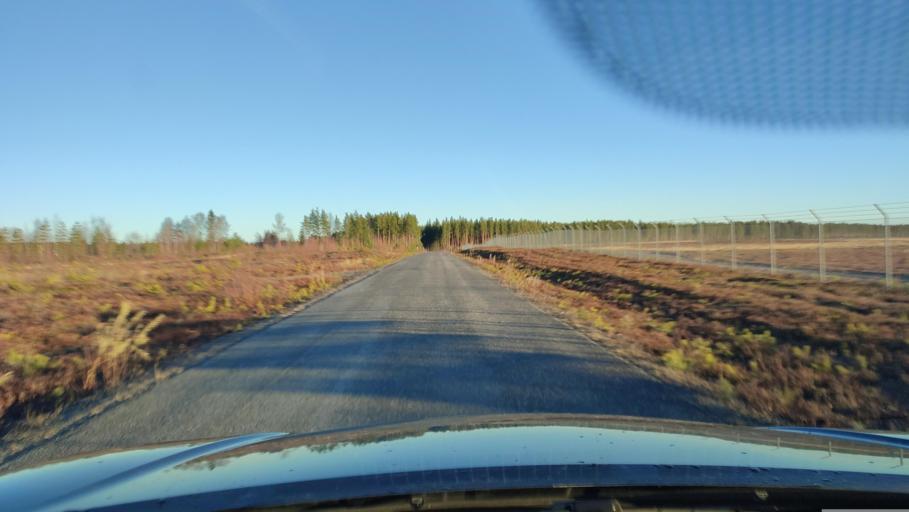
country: SE
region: Vaesterbotten
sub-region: Skelleftea Kommun
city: Soedra Bergsbyn
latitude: 64.6276
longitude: 21.0518
